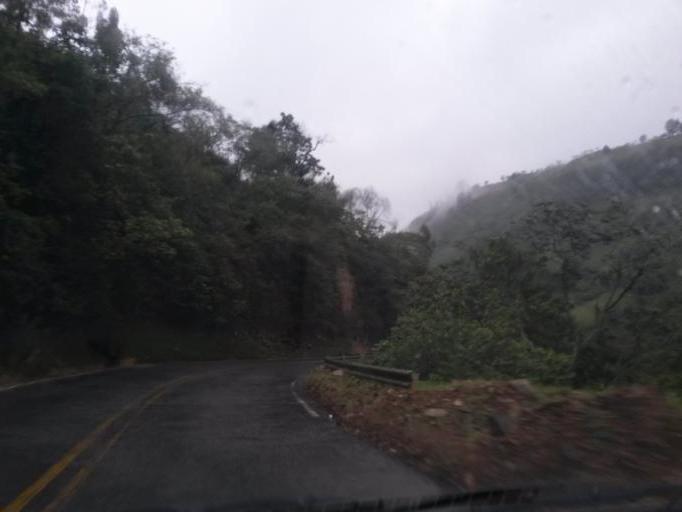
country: CO
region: Cauca
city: Popayan
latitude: 2.3879
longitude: -76.4947
